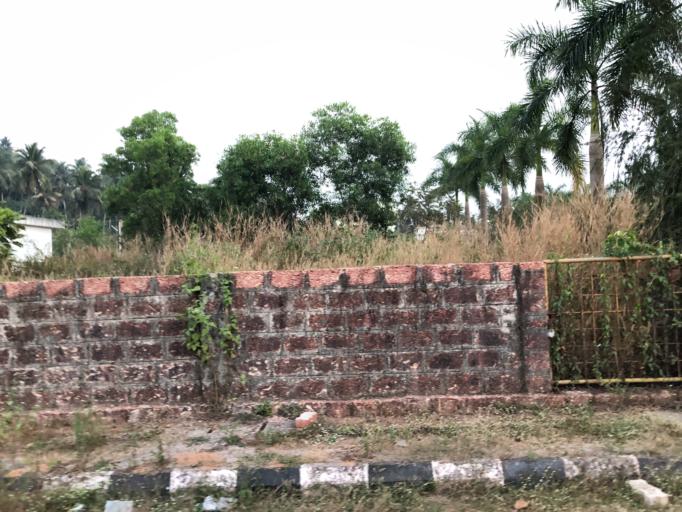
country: IN
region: Karnataka
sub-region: Dakshina Kannada
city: Mangalore
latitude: 12.8907
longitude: 74.8646
